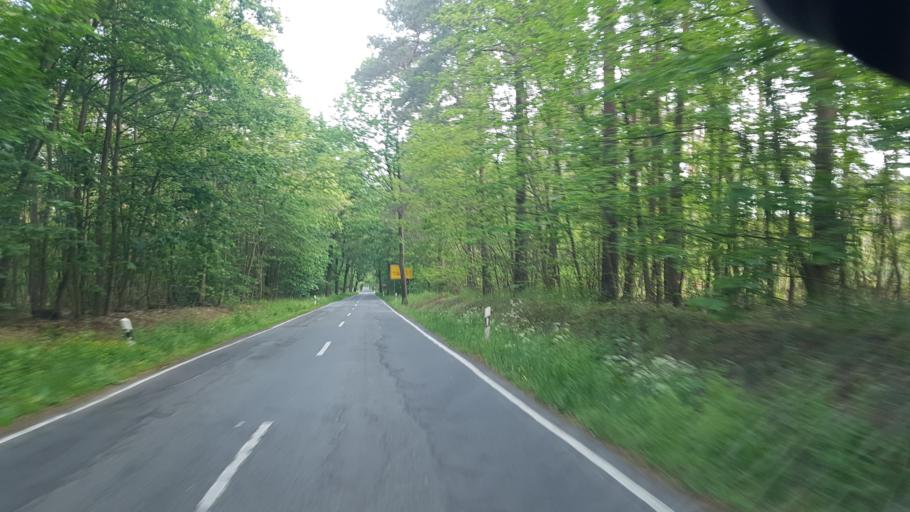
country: DE
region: Brandenburg
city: Baruth
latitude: 52.0225
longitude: 13.4694
